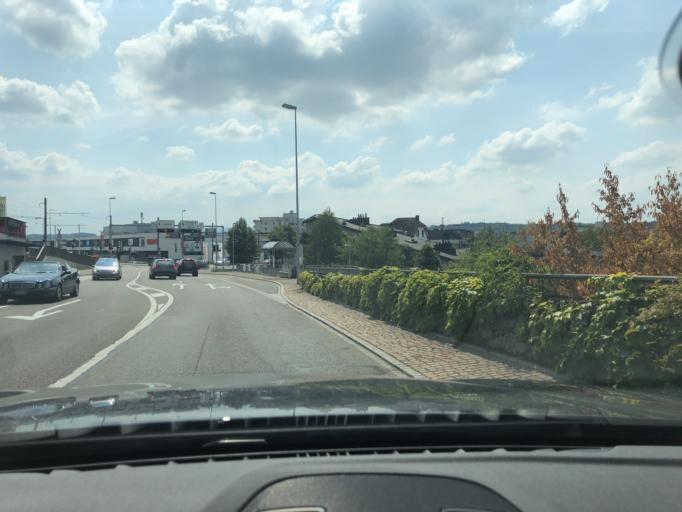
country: CH
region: Aargau
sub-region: Bezirk Bremgarten
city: Bremgarten
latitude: 47.3543
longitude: 8.3501
